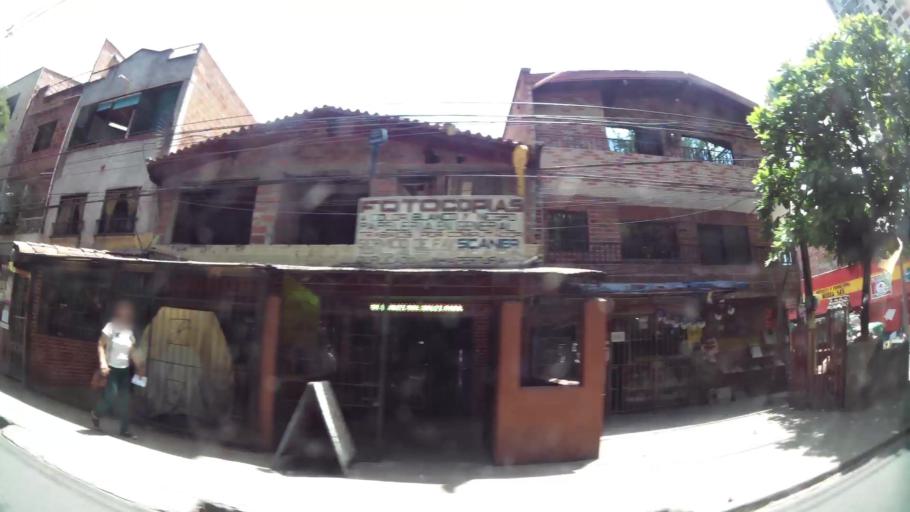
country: CO
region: Antioquia
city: Bello
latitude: 6.3380
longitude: -75.5497
